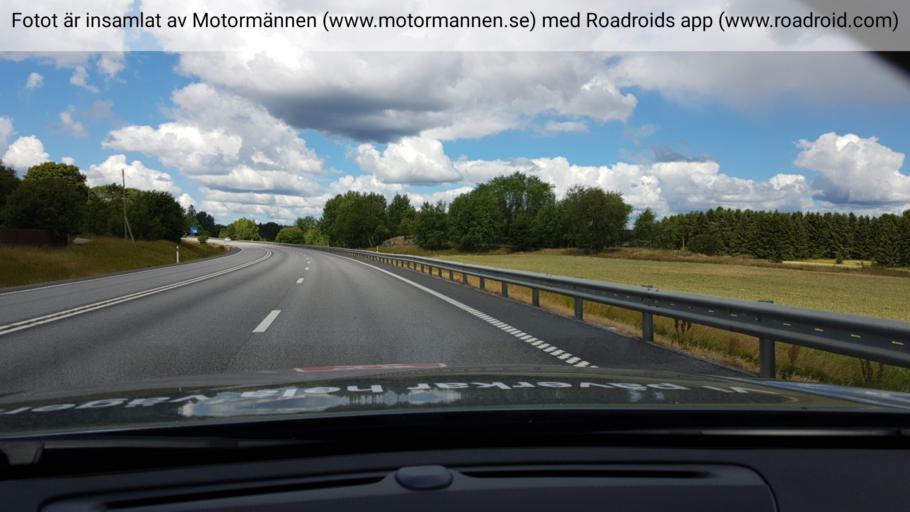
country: SE
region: Stockholm
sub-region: Osterakers Kommun
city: Akersberga
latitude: 59.4436
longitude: 18.2223
